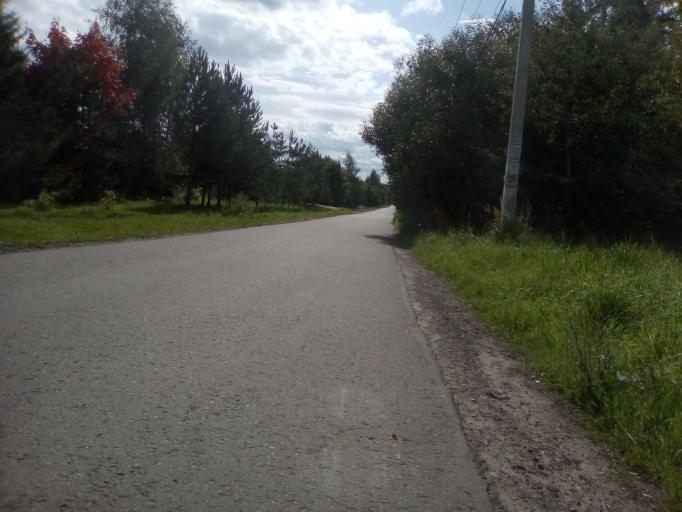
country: RU
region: Moskovskaya
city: Zhavoronki
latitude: 55.6472
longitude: 37.1439
